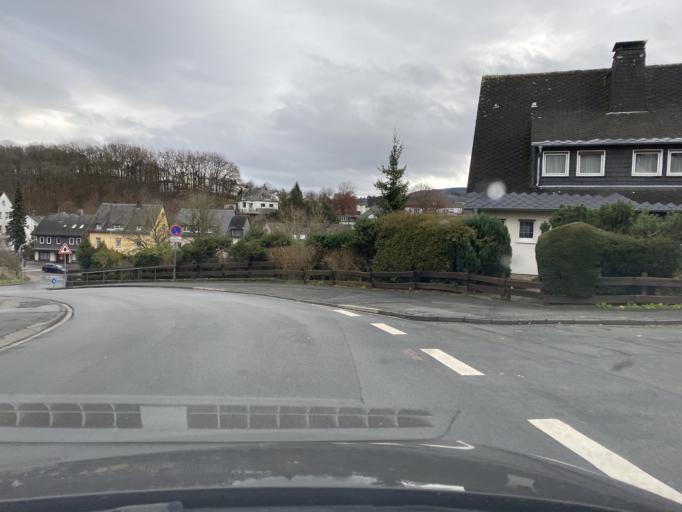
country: DE
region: North Rhine-Westphalia
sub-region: Regierungsbezirk Arnsberg
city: Meschede
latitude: 51.3520
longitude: 8.2792
